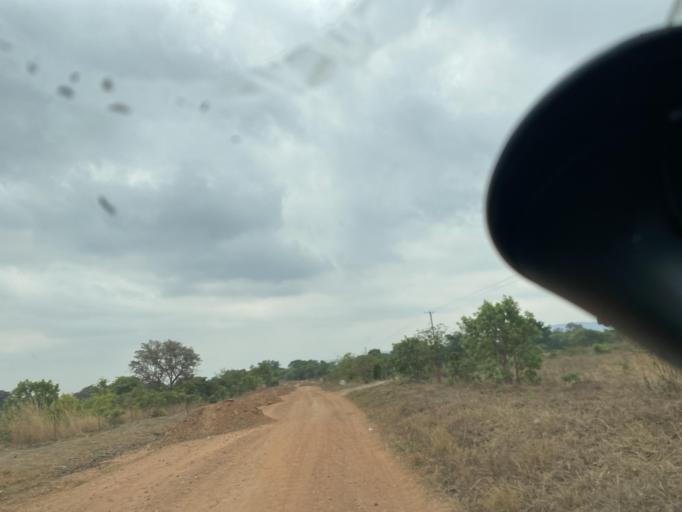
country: ZM
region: Lusaka
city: Chongwe
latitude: -15.2451
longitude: 28.7250
